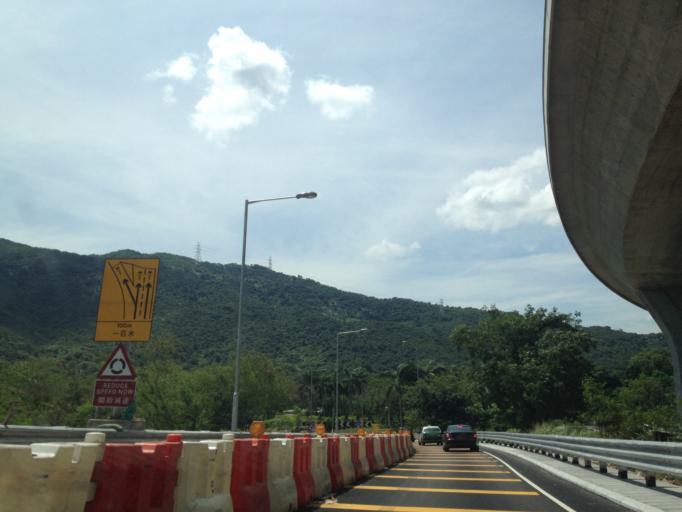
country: HK
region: Tai Po
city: Tai Po
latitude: 22.4593
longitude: 114.1472
